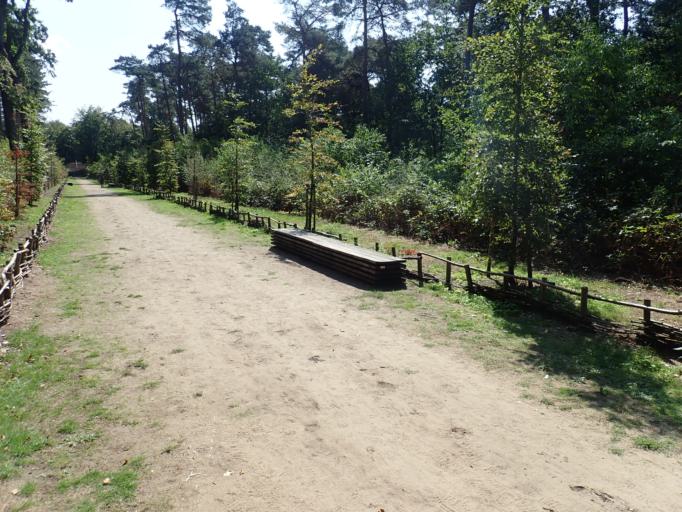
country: BE
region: Flanders
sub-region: Provincie Vlaams-Brabant
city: Scherpenheuvel-Zichem
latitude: 51.0314
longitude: 4.9813
